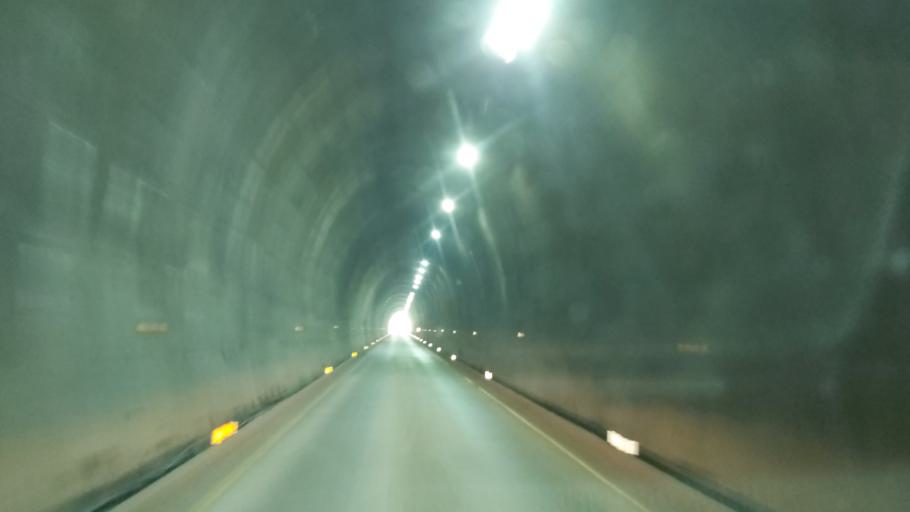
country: CL
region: Araucania
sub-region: Provincia de Cautin
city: Vilcun
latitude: -38.5542
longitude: -71.4999
